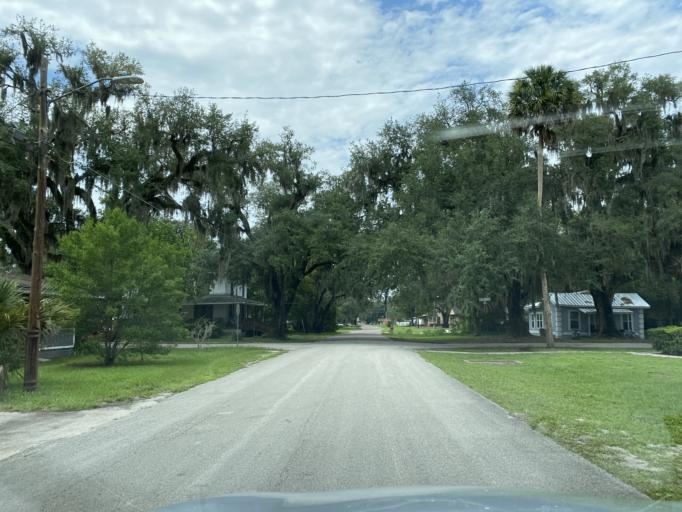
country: US
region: Florida
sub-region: Seminole County
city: Sanford
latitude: 28.8050
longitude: -81.2628
